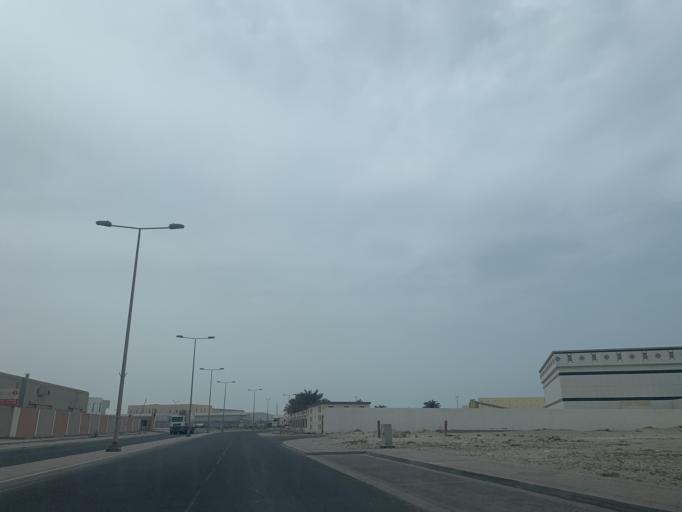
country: BH
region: Muharraq
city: Al Hadd
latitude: 26.2087
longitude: 50.6830
